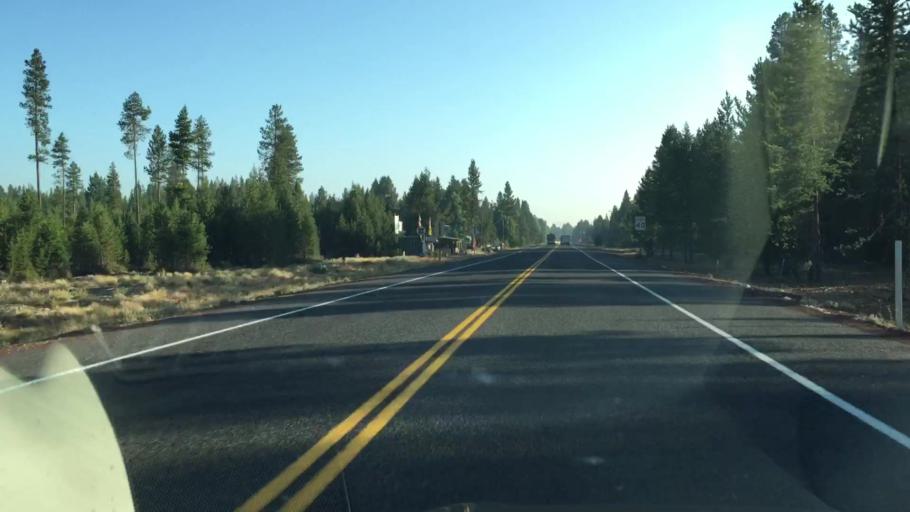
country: US
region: Oregon
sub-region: Deschutes County
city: La Pine
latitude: 43.4524
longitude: -121.7040
